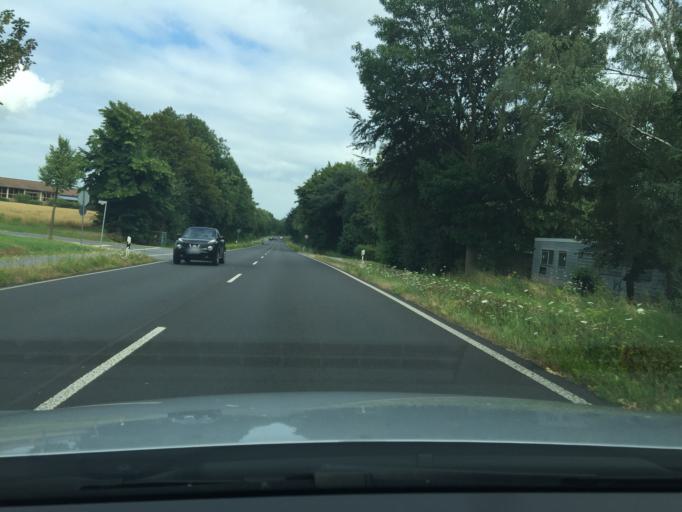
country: DE
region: North Rhine-Westphalia
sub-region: Regierungsbezirk Dusseldorf
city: Heiligenhaus
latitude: 51.3322
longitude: 6.9224
